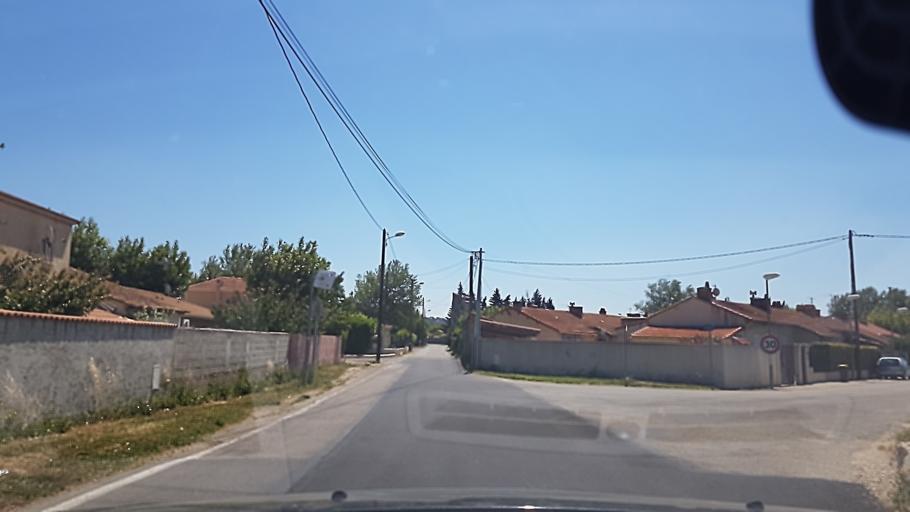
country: FR
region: Provence-Alpes-Cote d'Azur
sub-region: Departement du Vaucluse
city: Sorgues
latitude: 43.9894
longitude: 4.8741
